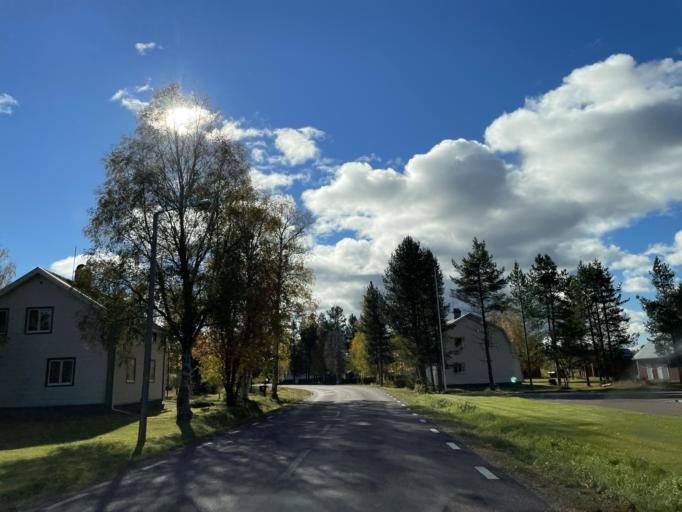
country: NO
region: Hedmark
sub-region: Trysil
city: Innbygda
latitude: 61.4103
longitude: 13.0834
